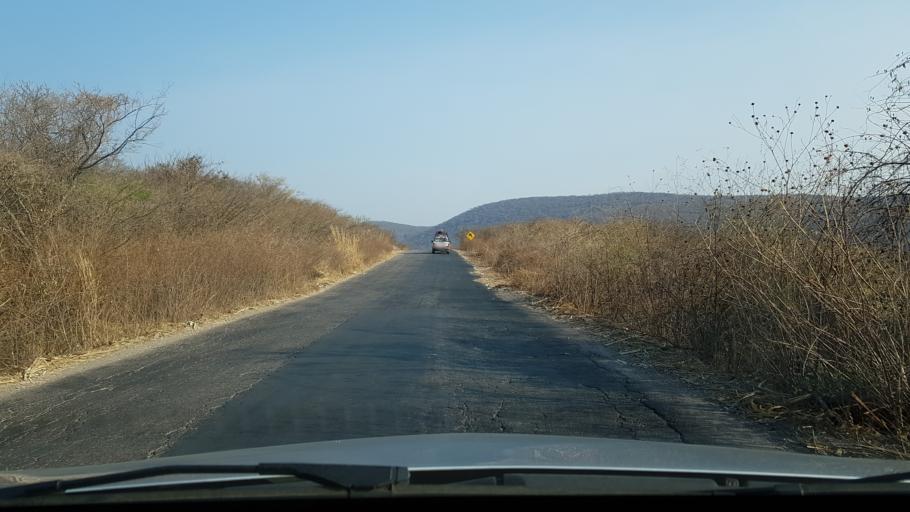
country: MX
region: Morelos
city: Tlaltizapan
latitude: 18.6685
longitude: -99.0534
